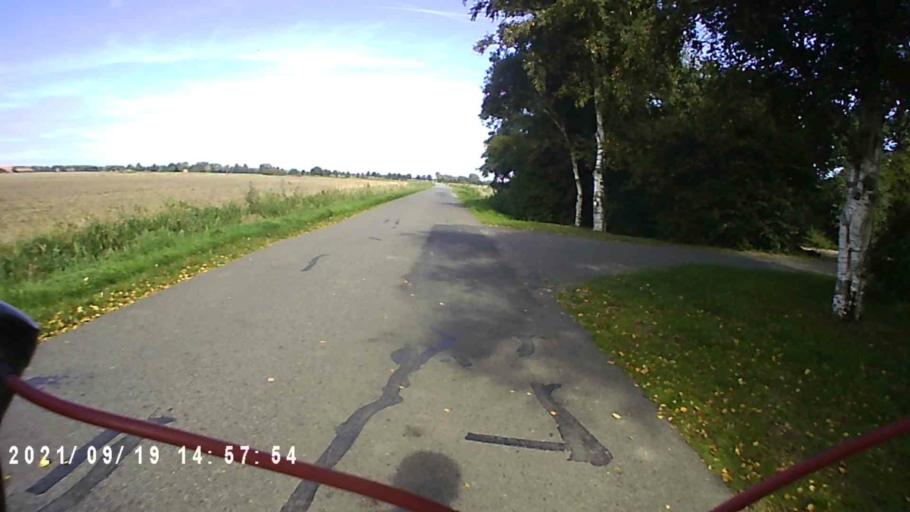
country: DE
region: Lower Saxony
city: Bunde
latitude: 53.1493
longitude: 7.2084
